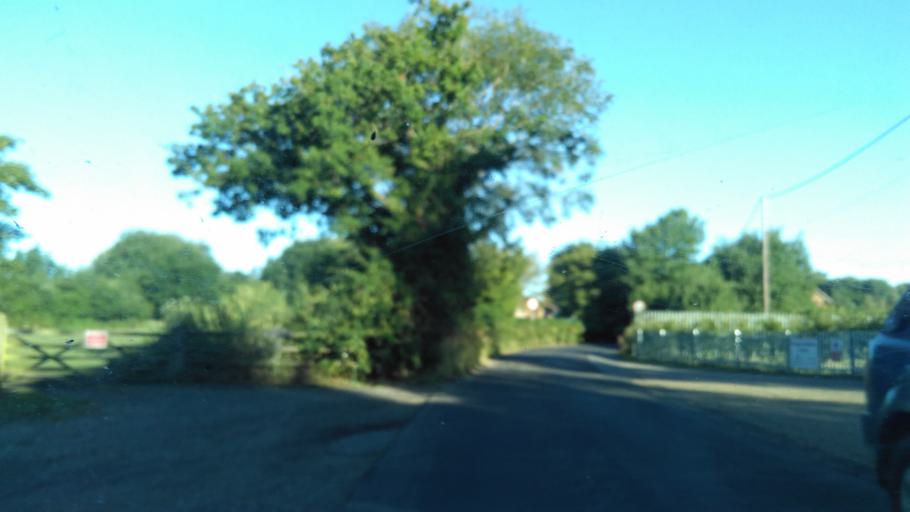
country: GB
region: England
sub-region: Kent
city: Chartham
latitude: 51.2690
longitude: 1.0191
